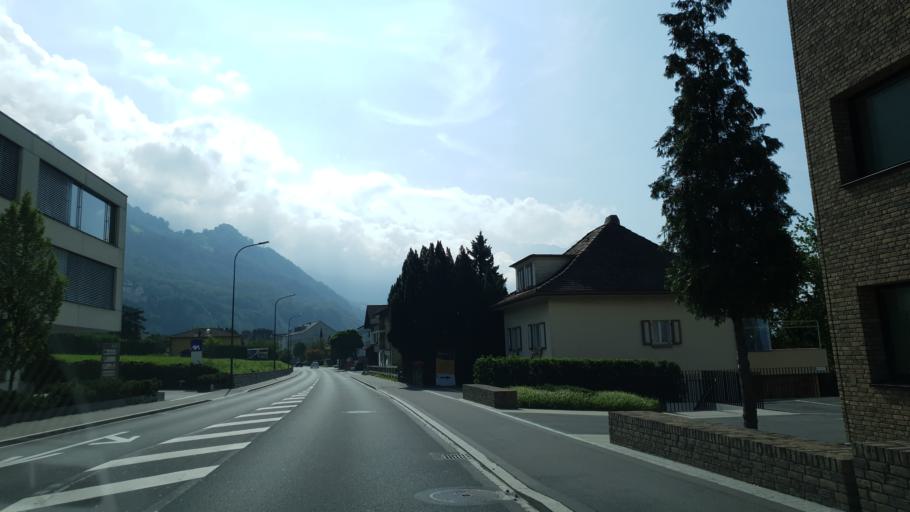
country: LI
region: Vaduz
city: Vaduz
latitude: 47.1470
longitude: 9.5134
